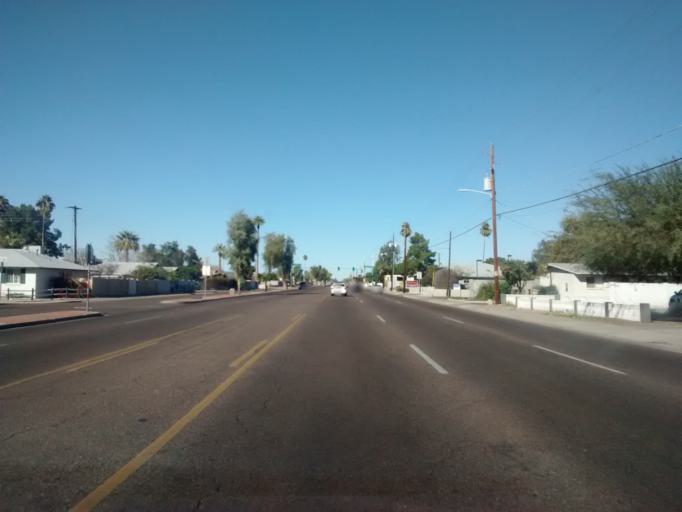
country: US
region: Arizona
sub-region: Maricopa County
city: Glendale
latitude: 33.5441
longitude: -112.1343
